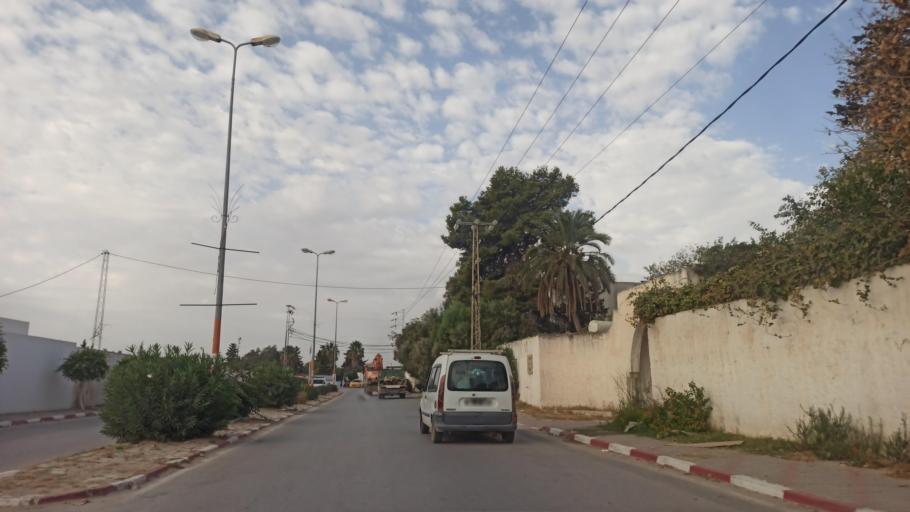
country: TN
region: Tunis
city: Al Marsa
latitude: 36.8736
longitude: 10.2701
